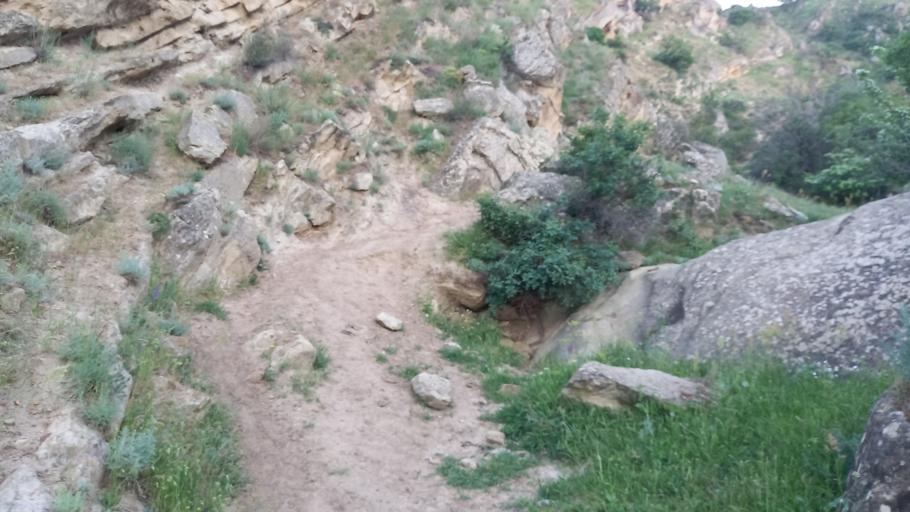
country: RU
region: Dagestan
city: Korkmaskala
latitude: 42.9800
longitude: 47.2444
